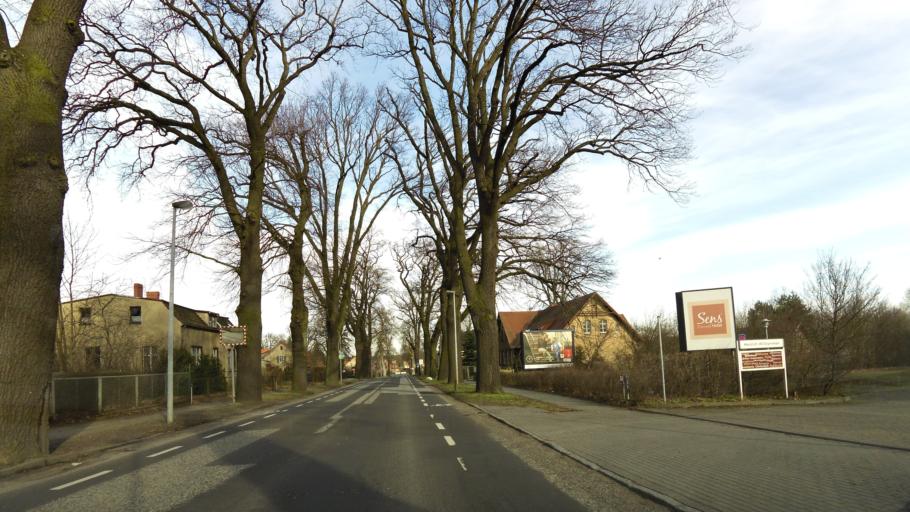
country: DE
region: Brandenburg
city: Michendorf
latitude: 52.3069
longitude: 13.0274
